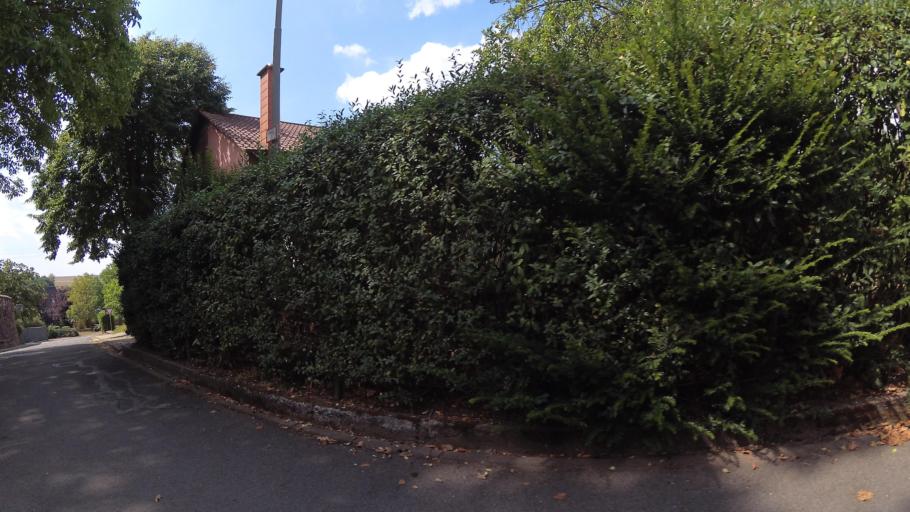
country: DE
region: Rheinland-Pfalz
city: Grossbundenbach
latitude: 49.3073
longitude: 7.4214
